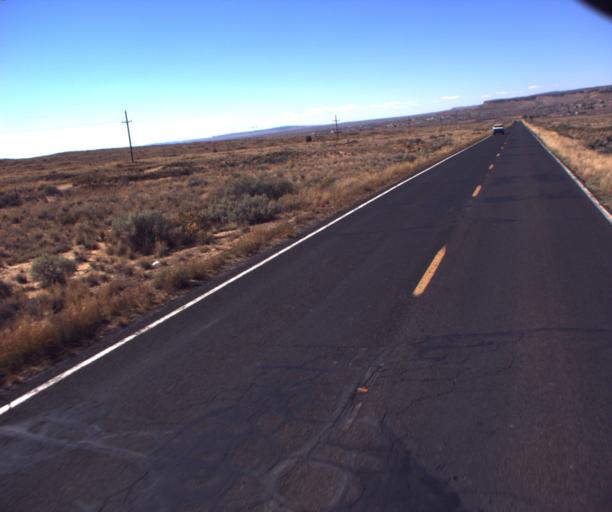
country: US
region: Arizona
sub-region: Navajo County
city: First Mesa
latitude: 35.8730
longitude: -110.5747
